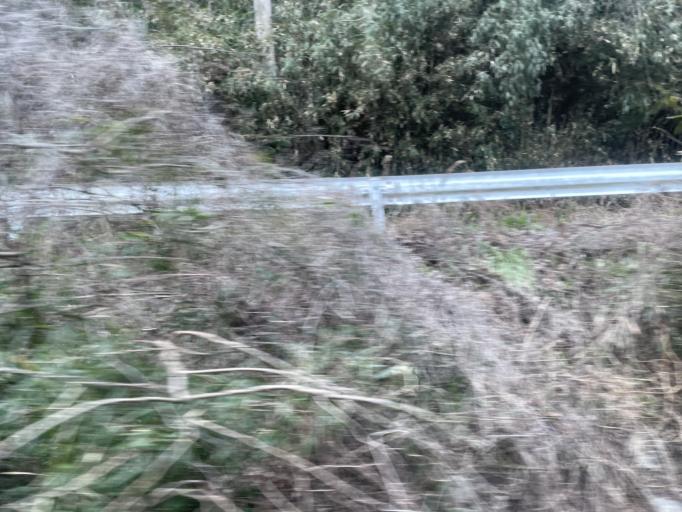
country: JP
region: Chiba
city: Narita
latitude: 35.8020
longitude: 140.2874
